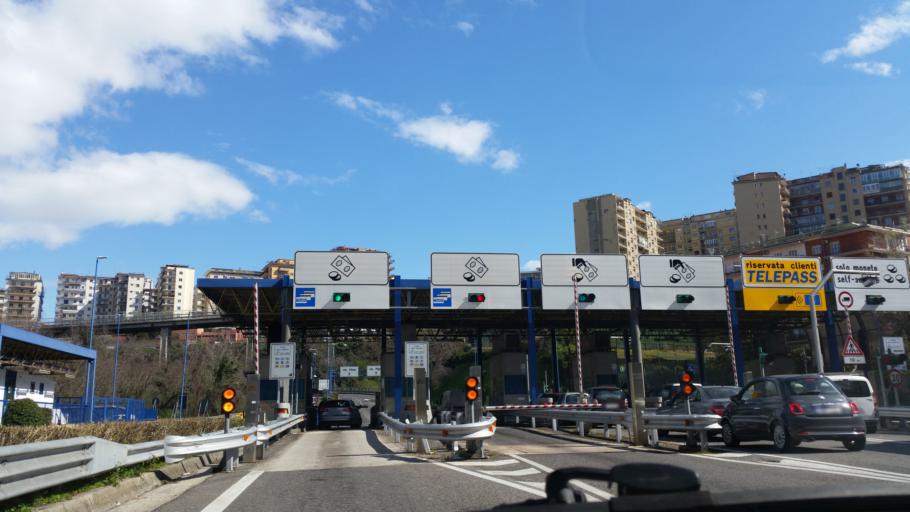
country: IT
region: Campania
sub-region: Provincia di Napoli
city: Napoli
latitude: 40.8436
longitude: 14.2155
